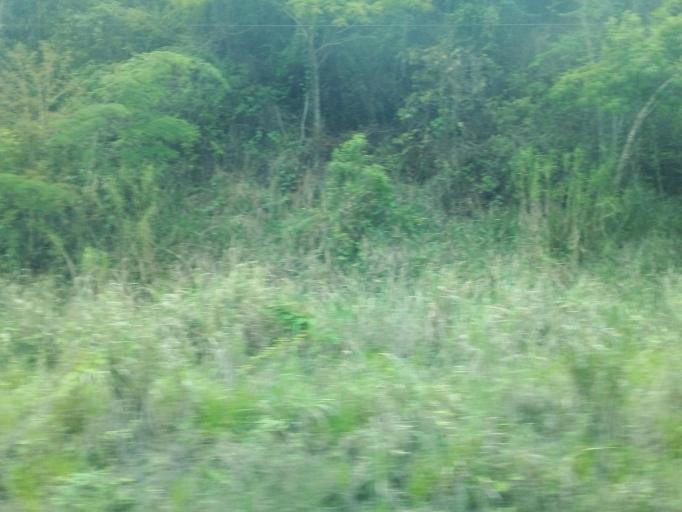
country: BR
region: Minas Gerais
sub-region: Nova Era
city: Nova Era
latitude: -19.7293
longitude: -42.9840
